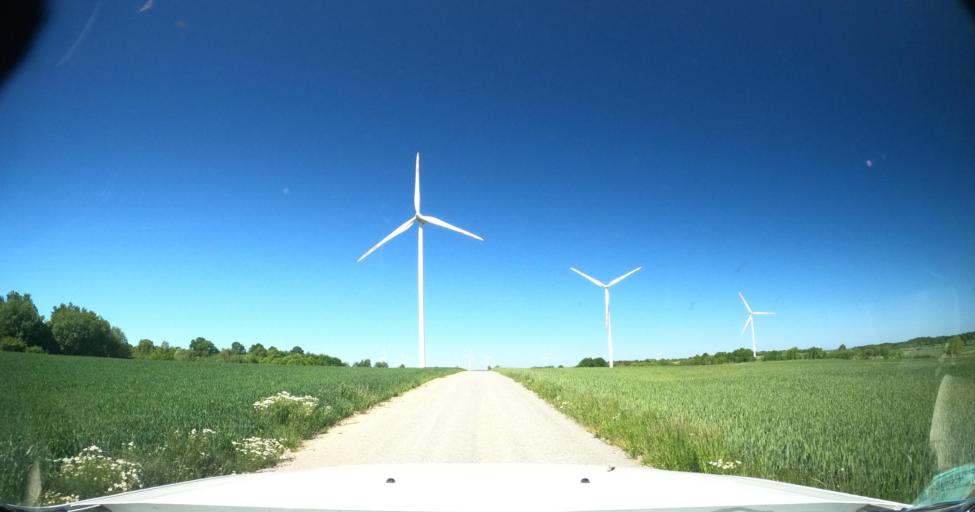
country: PL
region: Pomeranian Voivodeship
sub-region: Powiat slupski
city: Ustka
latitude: 54.5099
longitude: 16.7496
